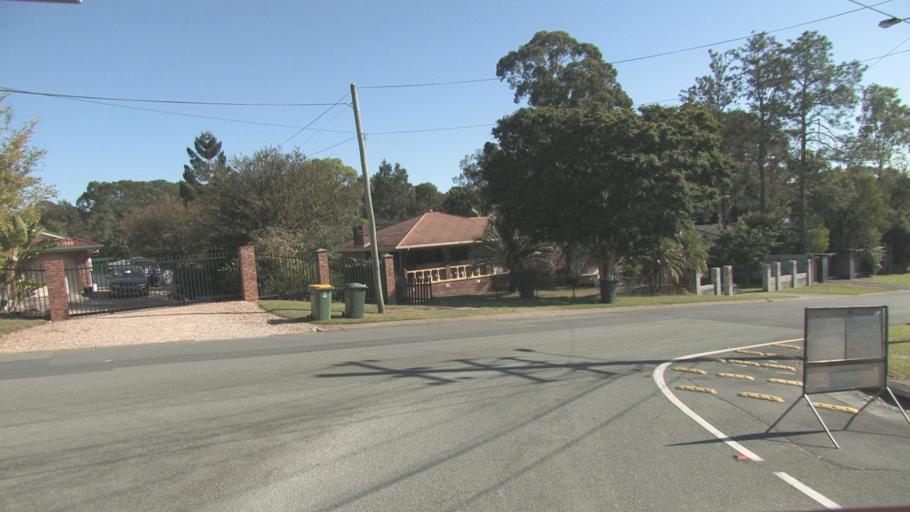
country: AU
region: Queensland
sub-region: Logan
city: Beenleigh
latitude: -27.7022
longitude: 153.1965
